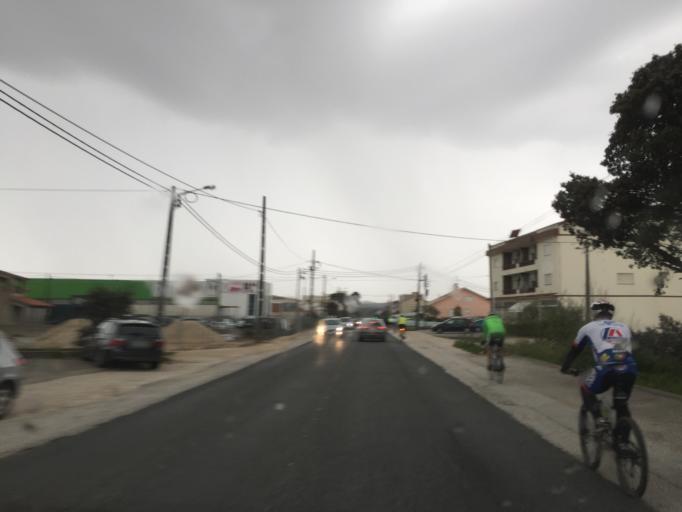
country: PT
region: Leiria
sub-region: Leiria
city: Santa Catarina da Serra
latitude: 39.6436
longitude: -8.6855
